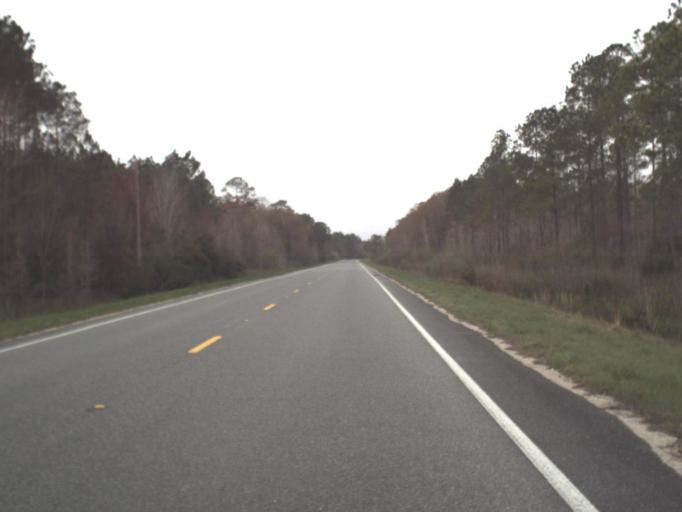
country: US
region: Florida
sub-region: Leon County
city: Woodville
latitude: 30.1927
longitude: -84.1111
